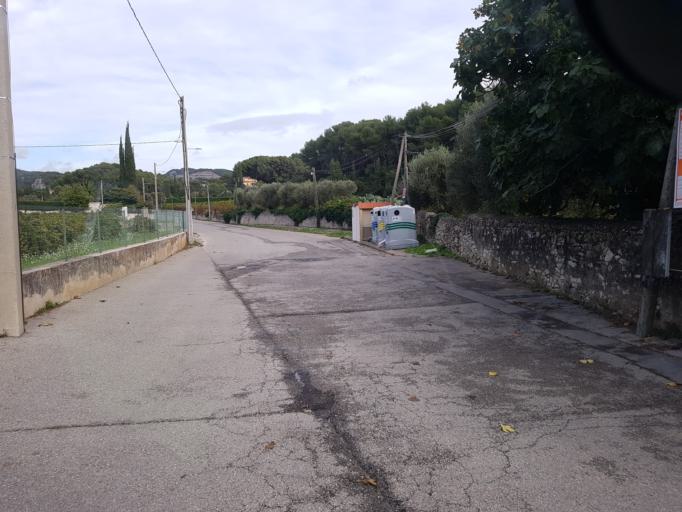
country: FR
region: Provence-Alpes-Cote d'Azur
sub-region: Departement des Bouches-du-Rhone
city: Cassis
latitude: 43.2198
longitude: 5.5536
